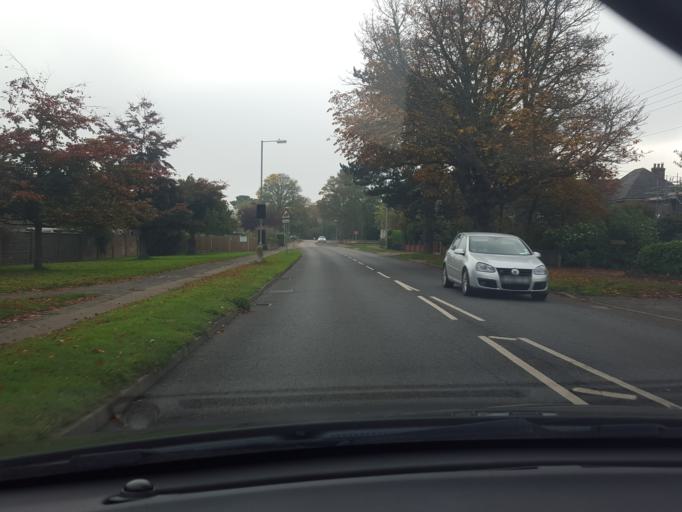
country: GB
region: England
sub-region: Essex
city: Brightlingsea
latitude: 51.8207
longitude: 1.0185
